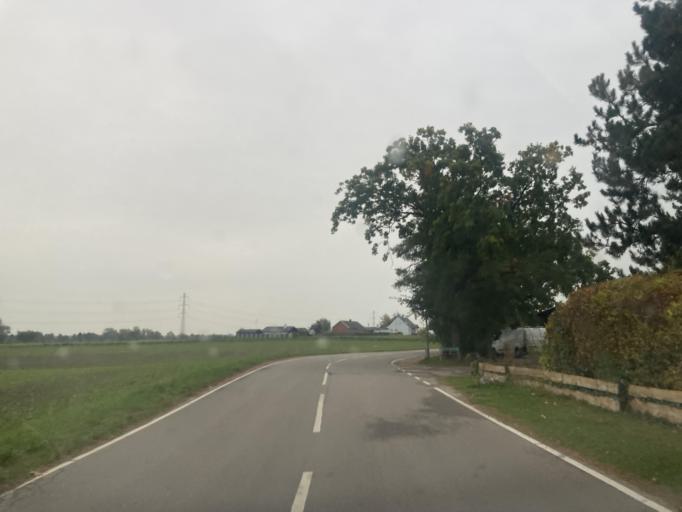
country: DK
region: Capital Region
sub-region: Egedal Kommune
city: Vekso
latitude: 55.7150
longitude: 12.2162
